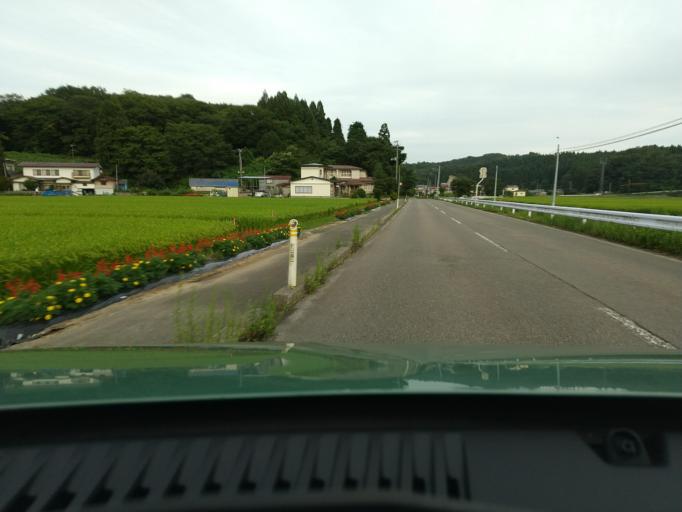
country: JP
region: Akita
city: Akita
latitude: 39.7819
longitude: 140.1310
